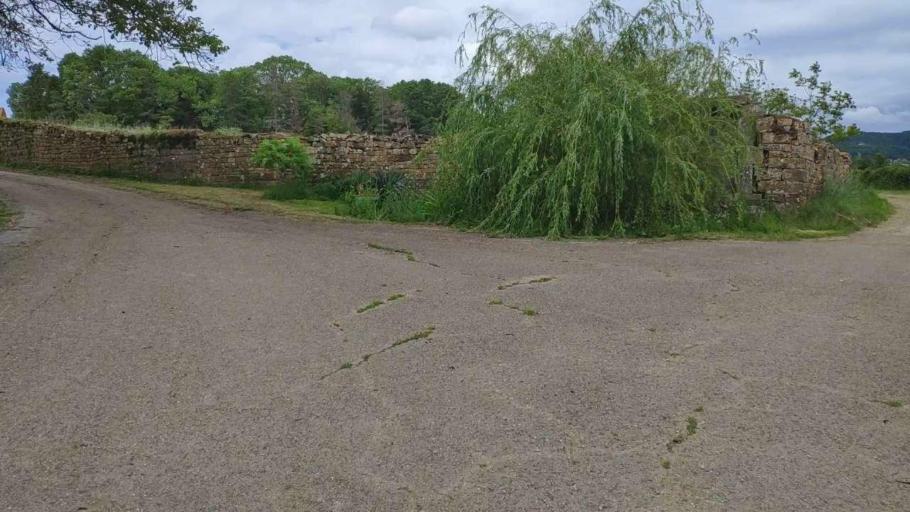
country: FR
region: Franche-Comte
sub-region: Departement du Jura
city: Perrigny
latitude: 46.7776
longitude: 5.5770
